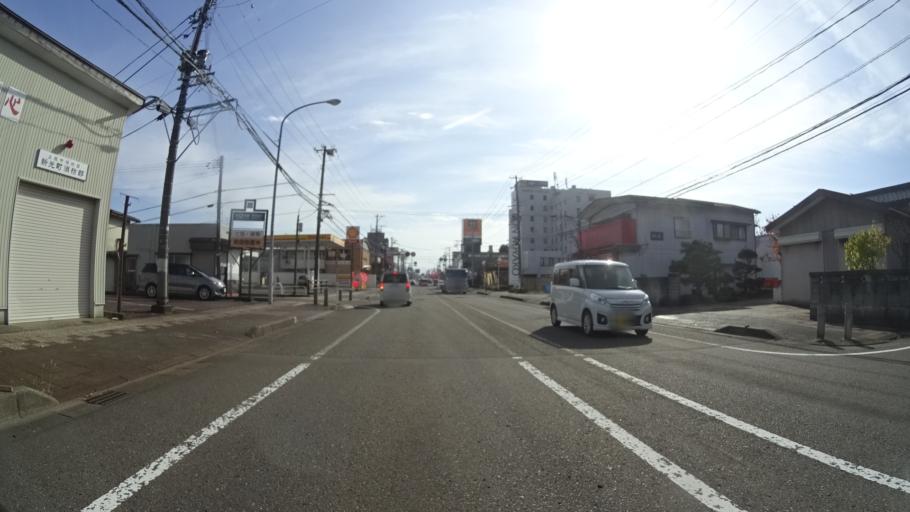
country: JP
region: Niigata
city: Joetsu
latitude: 37.1529
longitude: 138.2385
